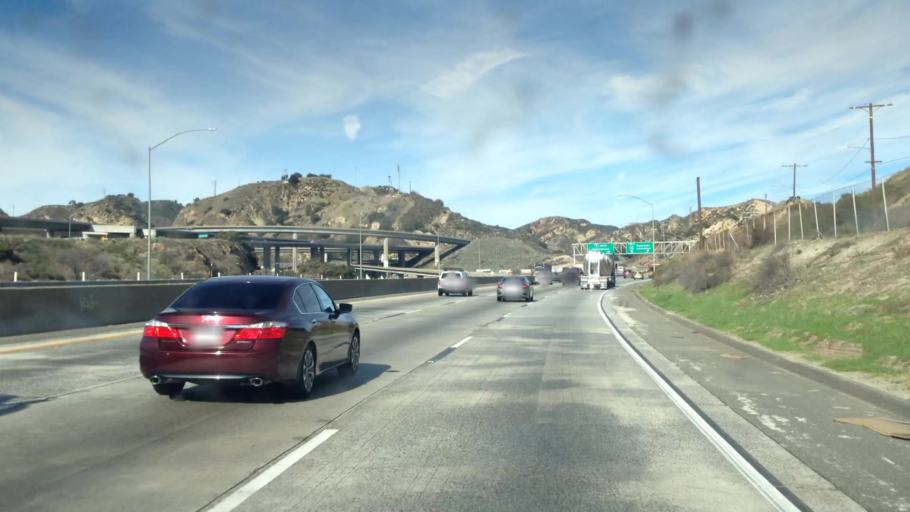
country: US
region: California
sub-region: Los Angeles County
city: Santa Clarita
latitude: 34.3301
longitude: -118.5038
